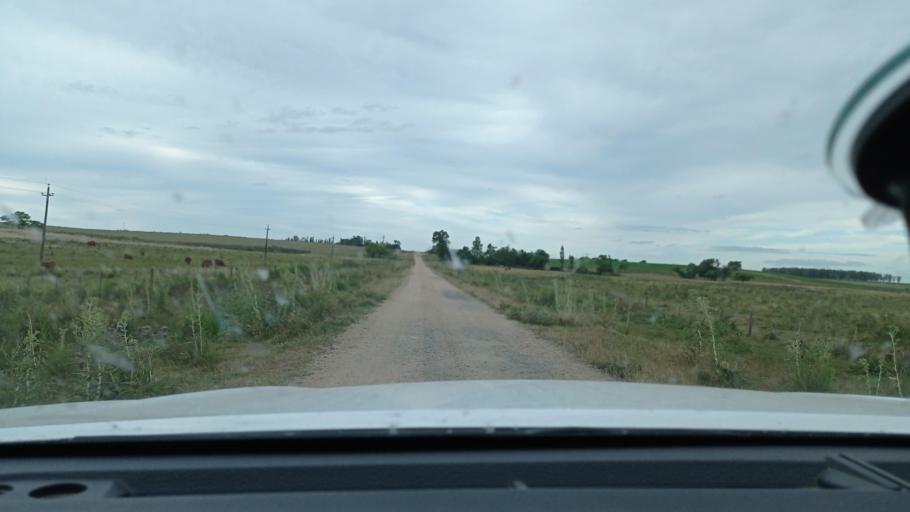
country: UY
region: Florida
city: Casupa
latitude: -34.1216
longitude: -55.7715
